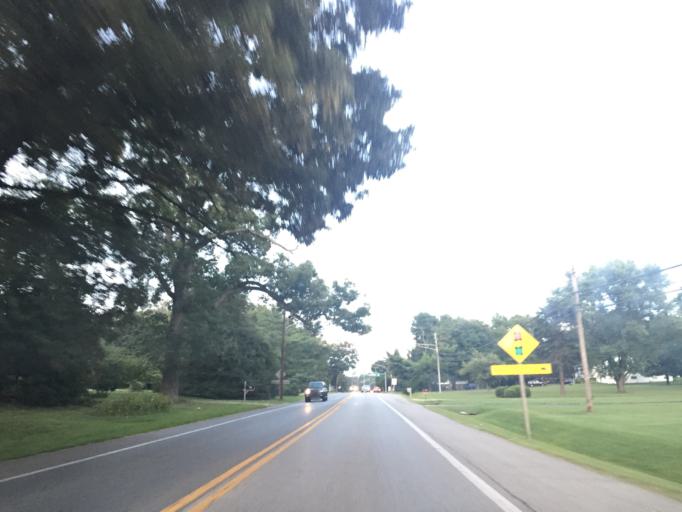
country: US
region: Maryland
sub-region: Anne Arundel County
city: Gambrills
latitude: 39.0697
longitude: -76.6724
